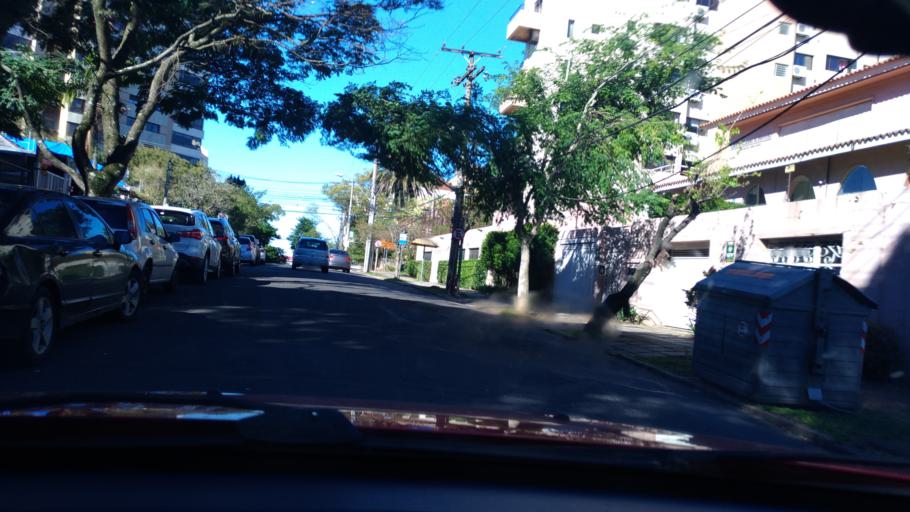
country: BR
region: Rio Grande do Sul
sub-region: Porto Alegre
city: Porto Alegre
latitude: -30.0187
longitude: -51.1858
